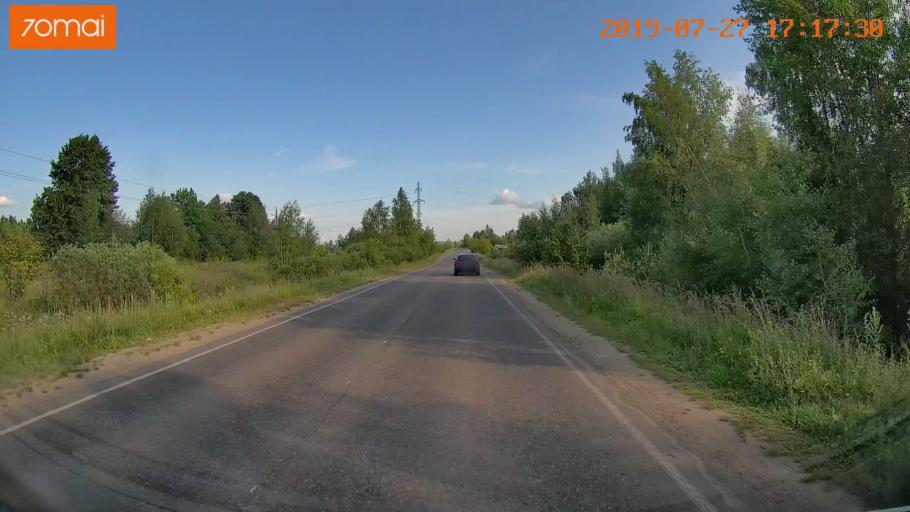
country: RU
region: Ivanovo
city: Novo-Talitsy
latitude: 57.0367
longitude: 40.8952
